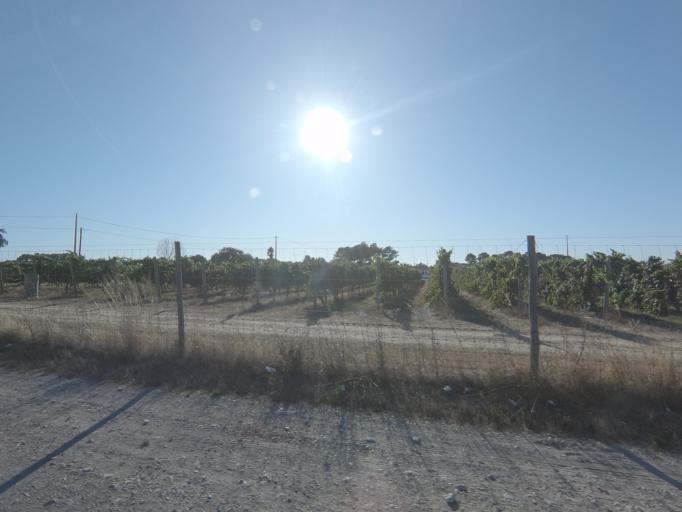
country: PT
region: Setubal
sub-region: Palmela
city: Quinta do Anjo
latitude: 38.5395
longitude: -8.9863
